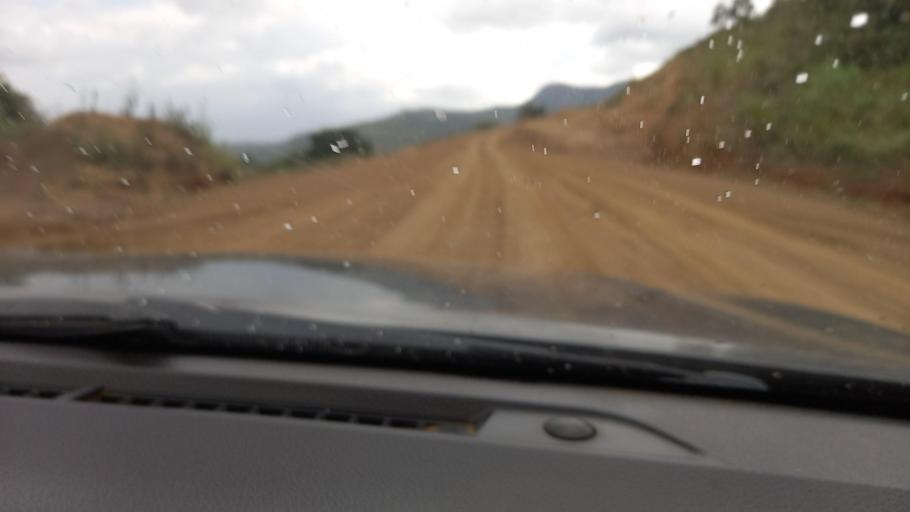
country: ET
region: Southern Nations, Nationalities, and People's Region
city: Mizan Teferi
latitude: 6.2071
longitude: 35.6681
